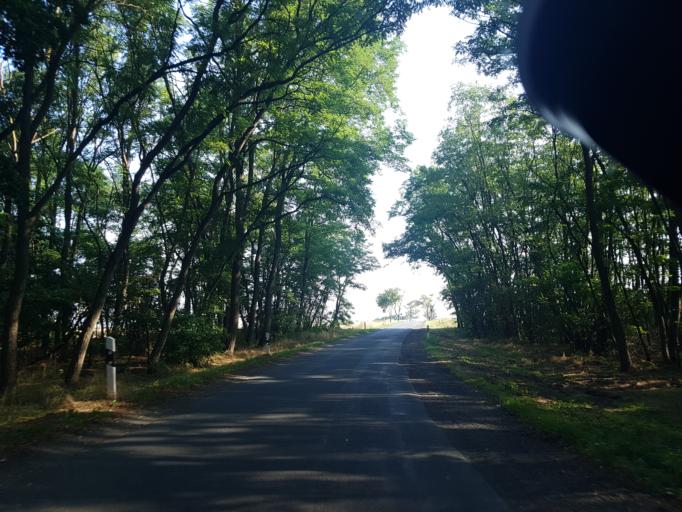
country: DE
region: Brandenburg
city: Niemegk
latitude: 52.0071
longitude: 12.6823
